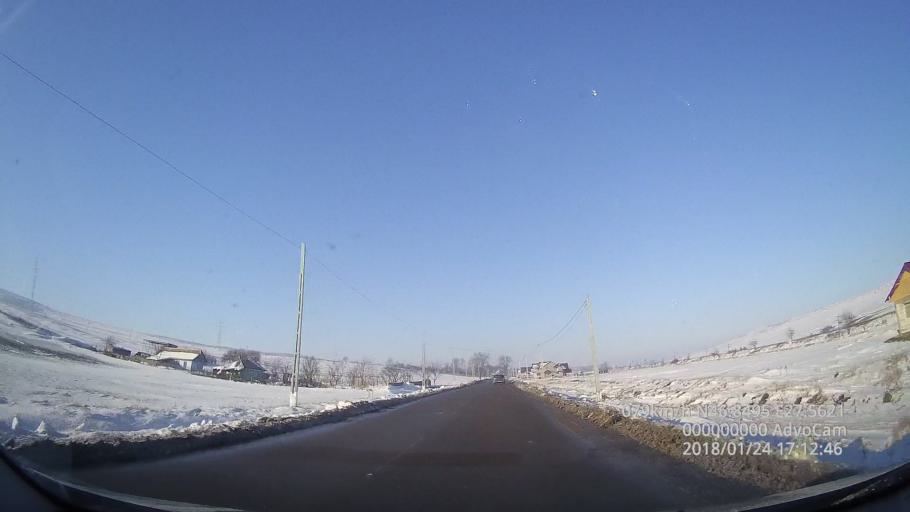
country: RO
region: Vaslui
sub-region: Comuna Rebricea
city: Rebricea
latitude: 46.8503
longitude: 27.5620
